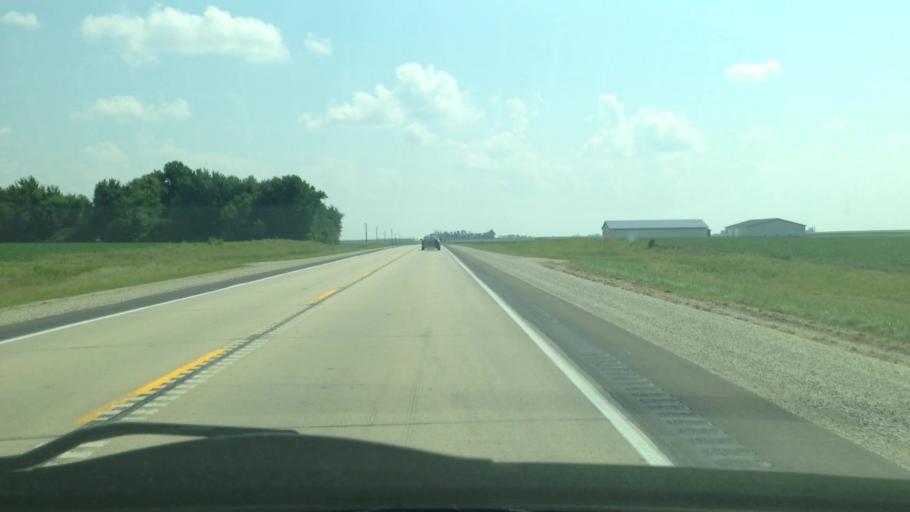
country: US
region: Iowa
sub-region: Howard County
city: Cresco
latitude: 43.4239
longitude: -92.2986
